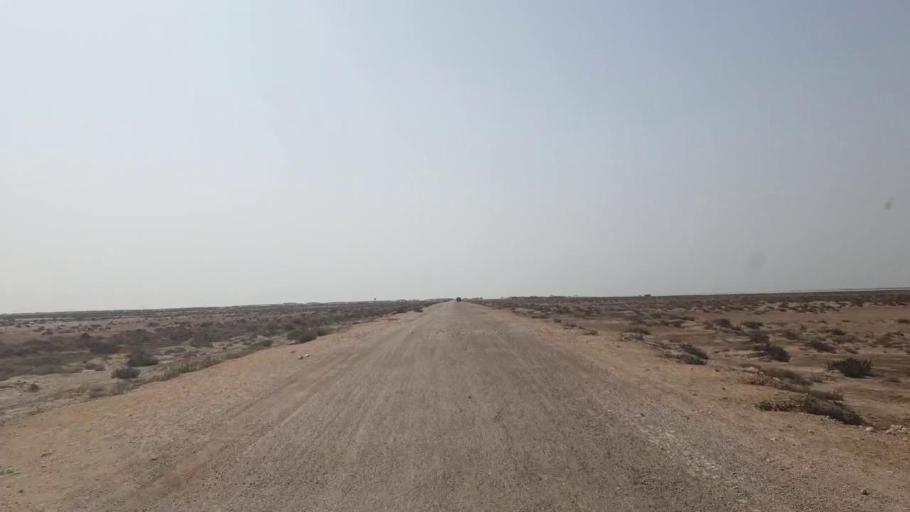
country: PK
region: Sindh
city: Jati
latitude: 24.3508
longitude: 68.5937
